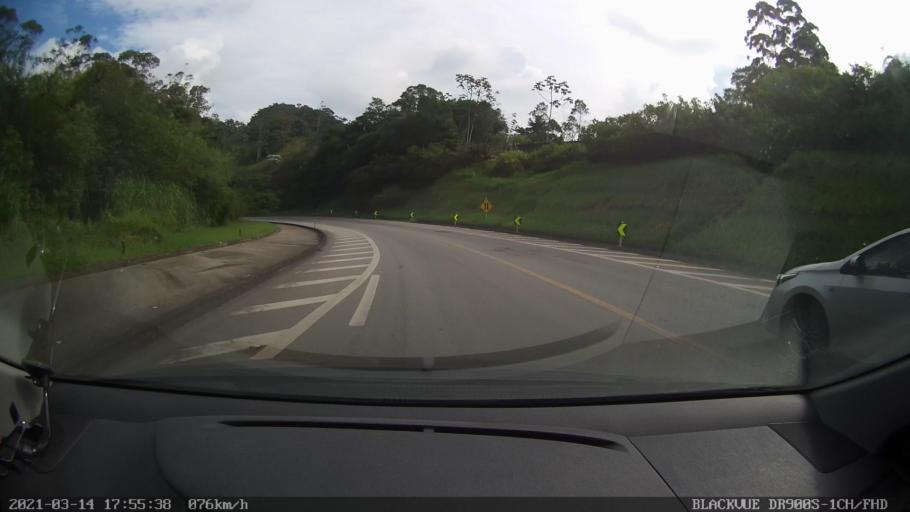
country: BR
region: Rio de Janeiro
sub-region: Petropolis
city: Petropolis
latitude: -22.4993
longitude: -43.2306
